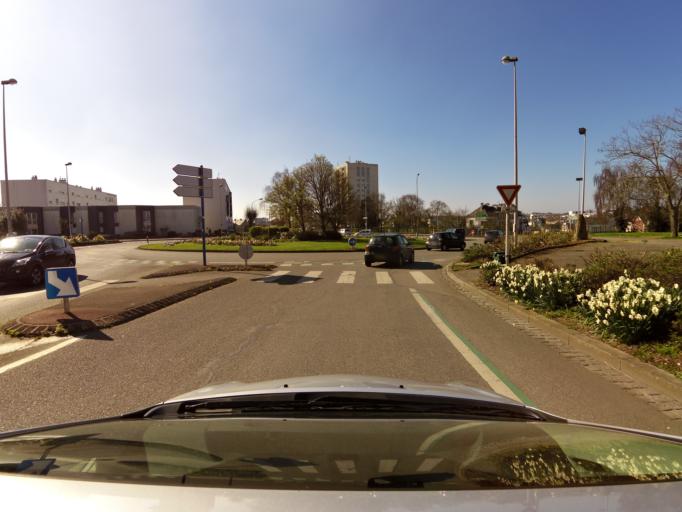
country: FR
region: Brittany
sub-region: Departement du Morbihan
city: Lorient
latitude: 47.7398
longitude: -3.3799
